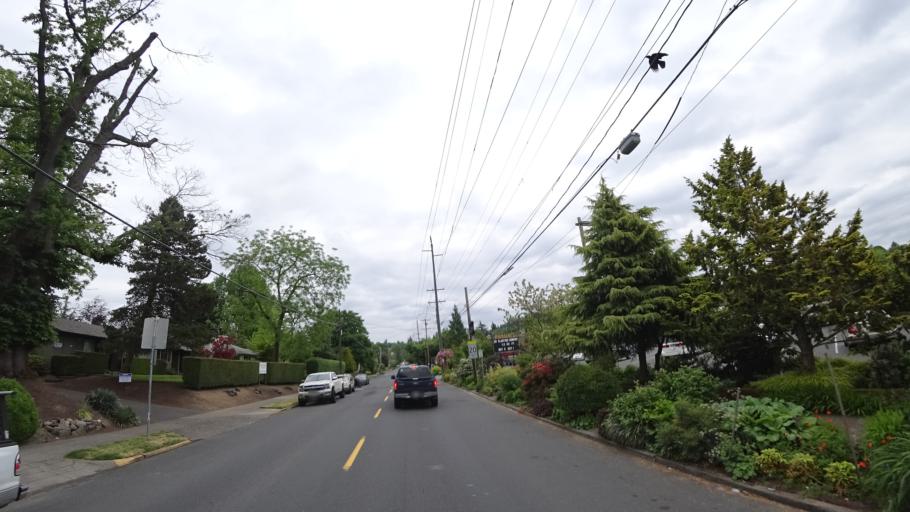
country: US
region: Oregon
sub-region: Multnomah County
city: Lents
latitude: 45.5193
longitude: -122.6115
